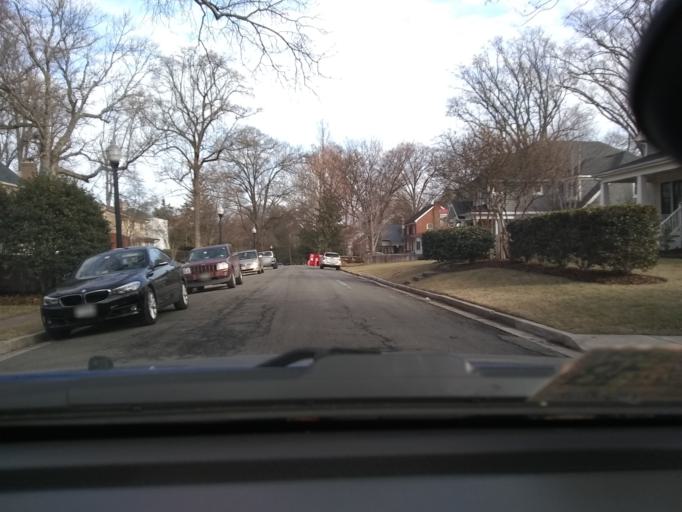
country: US
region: Virginia
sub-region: Arlington County
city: Arlington
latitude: 38.8872
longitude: -77.1246
